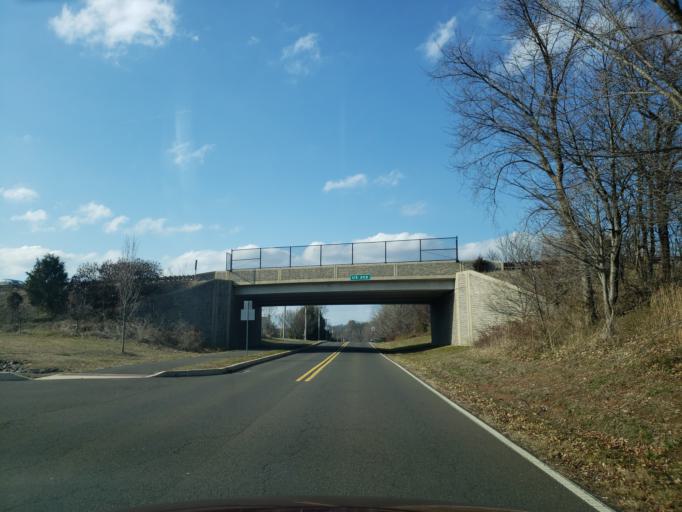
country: US
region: Pennsylvania
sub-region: Bucks County
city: Doylestown
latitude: 40.2914
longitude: -75.1412
